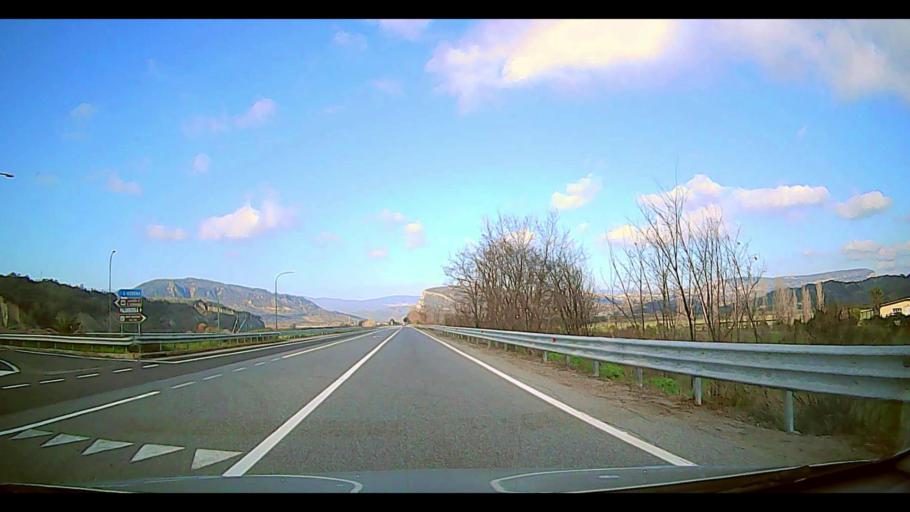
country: IT
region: Calabria
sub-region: Provincia di Crotone
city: Santa Severina
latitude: 39.1752
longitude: 16.9327
